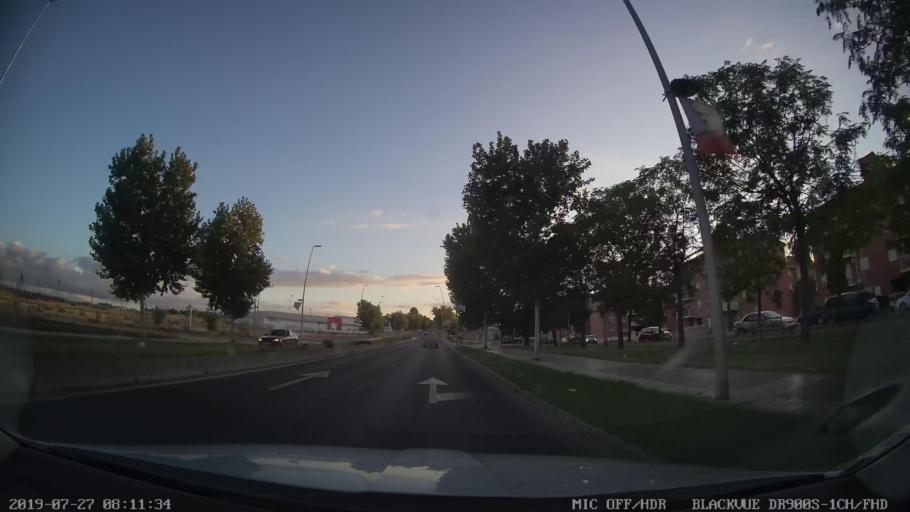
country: ES
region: Extremadura
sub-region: Provincia de Badajoz
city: Merida
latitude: 38.9058
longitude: -6.3571
